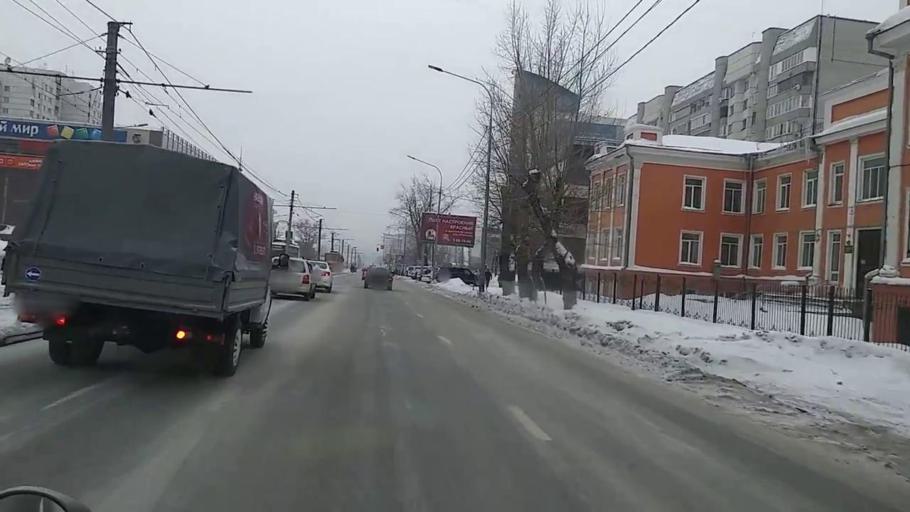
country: RU
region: Altai Krai
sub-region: Gorod Barnaulskiy
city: Barnaul
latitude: 53.3389
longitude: 83.7730
